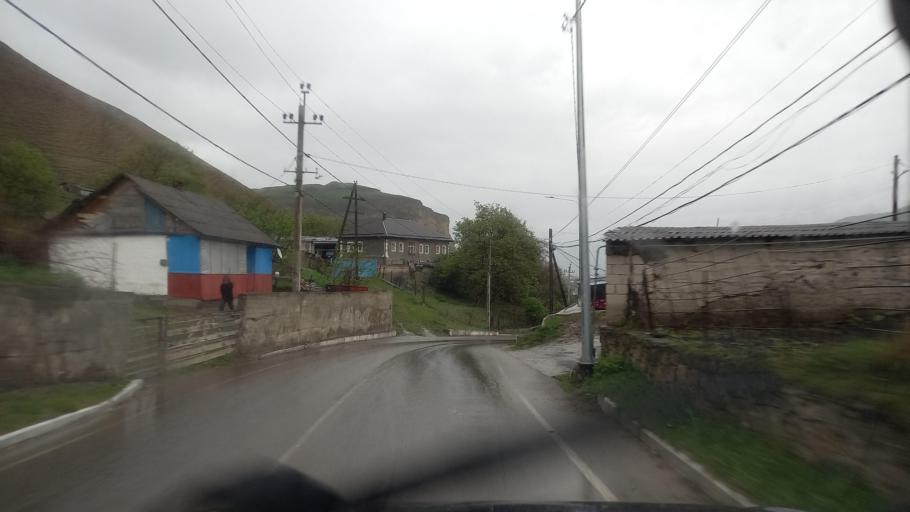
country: RU
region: Kabardino-Balkariya
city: Gundelen
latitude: 43.5994
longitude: 43.1574
